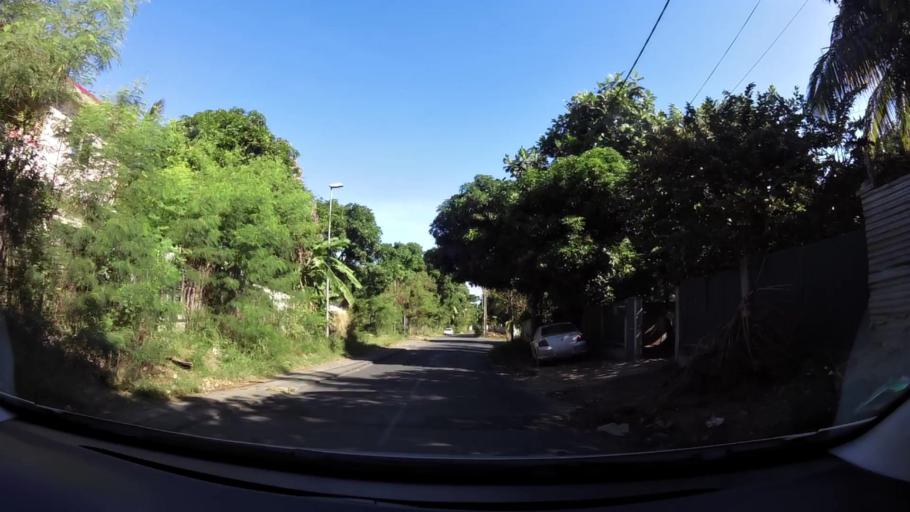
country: YT
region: Pamandzi
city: Pamandzi
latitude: -12.7933
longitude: 45.2798
